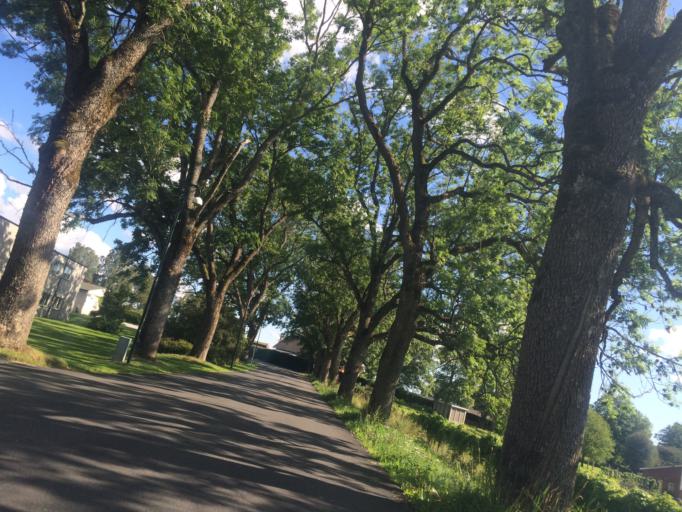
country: NO
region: Akershus
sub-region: As
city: As
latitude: 59.6701
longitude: 10.7701
